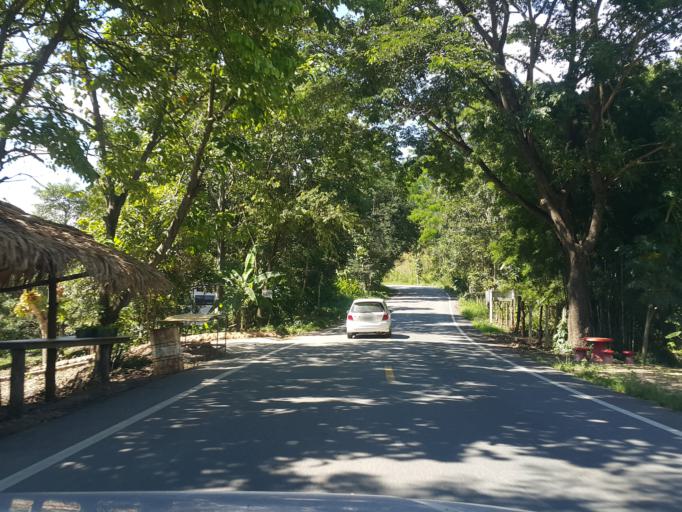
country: TH
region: Chiang Mai
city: Mae Taeng
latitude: 19.1817
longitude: 98.9108
